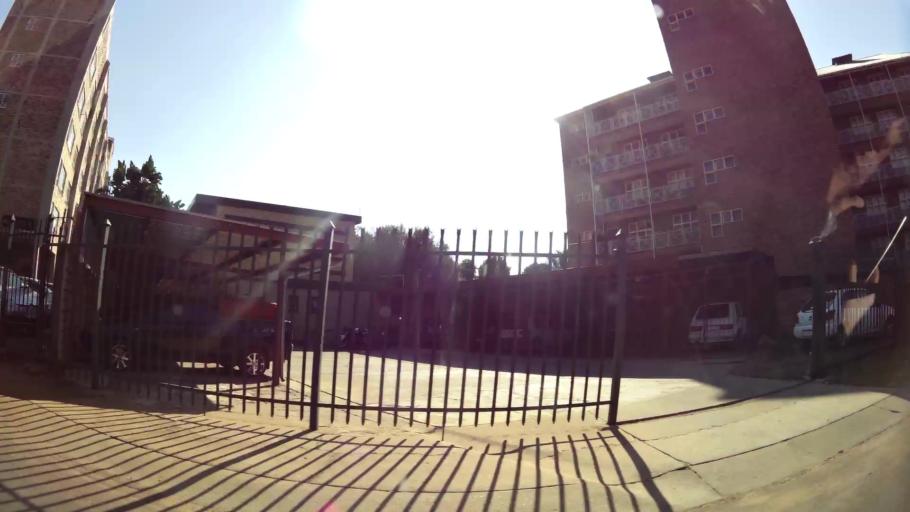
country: ZA
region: Gauteng
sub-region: City of Tshwane Metropolitan Municipality
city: Pretoria
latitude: -25.6792
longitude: 28.1716
